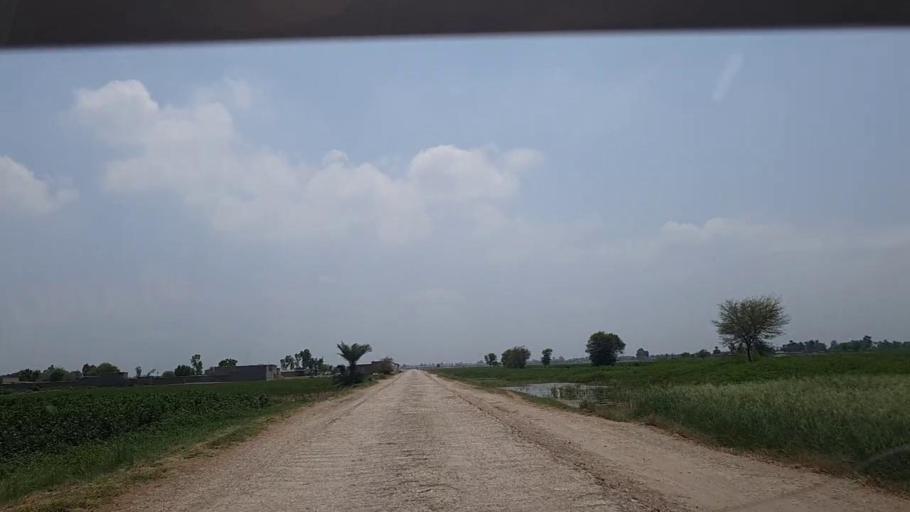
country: PK
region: Sindh
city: Khanpur
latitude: 27.9048
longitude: 69.3918
